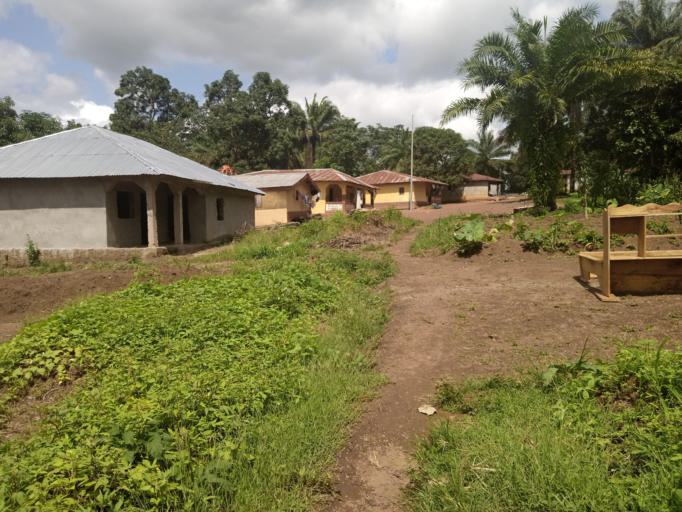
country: SL
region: Northern Province
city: Kamakwie
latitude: 9.4952
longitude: -12.2469
